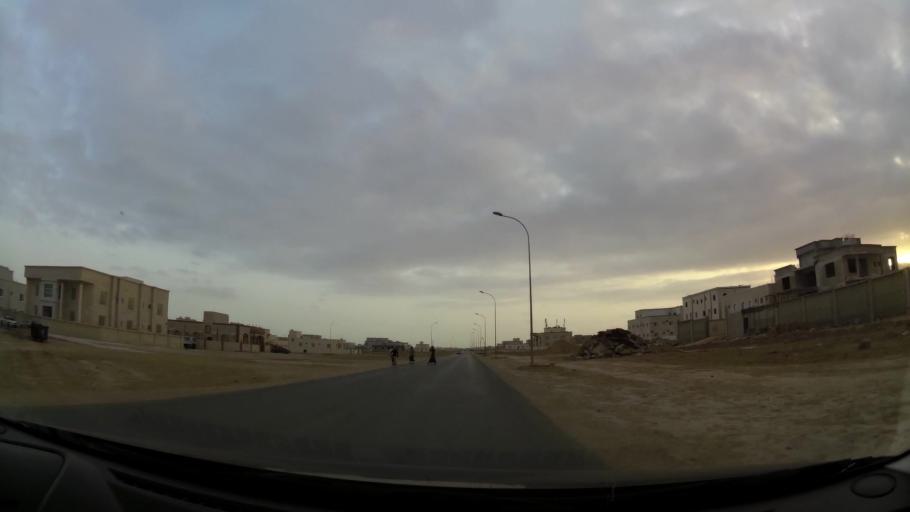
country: OM
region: Zufar
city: Salalah
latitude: 17.0386
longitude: 54.0202
